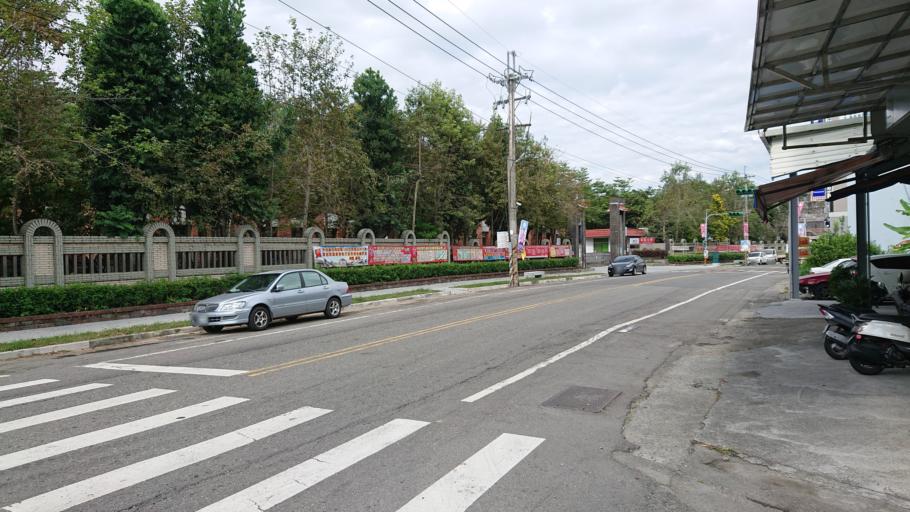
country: TW
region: Taiwan
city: Lugu
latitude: 23.7513
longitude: 120.6789
